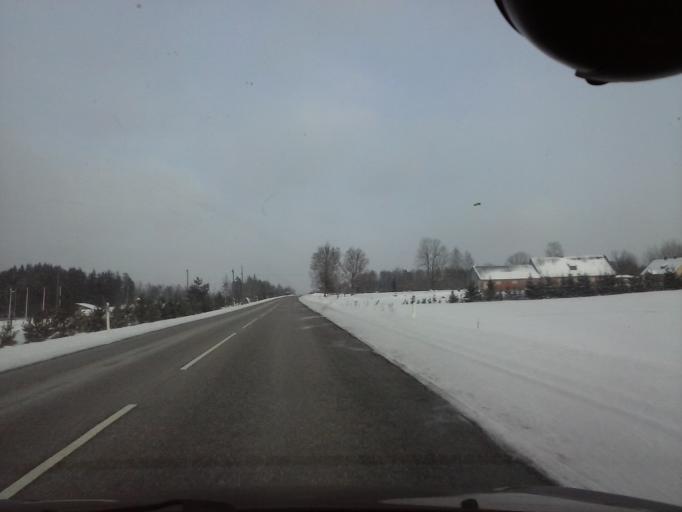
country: EE
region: Paernumaa
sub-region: Saarde vald
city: Kilingi-Nomme
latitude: 58.1662
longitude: 25.0182
